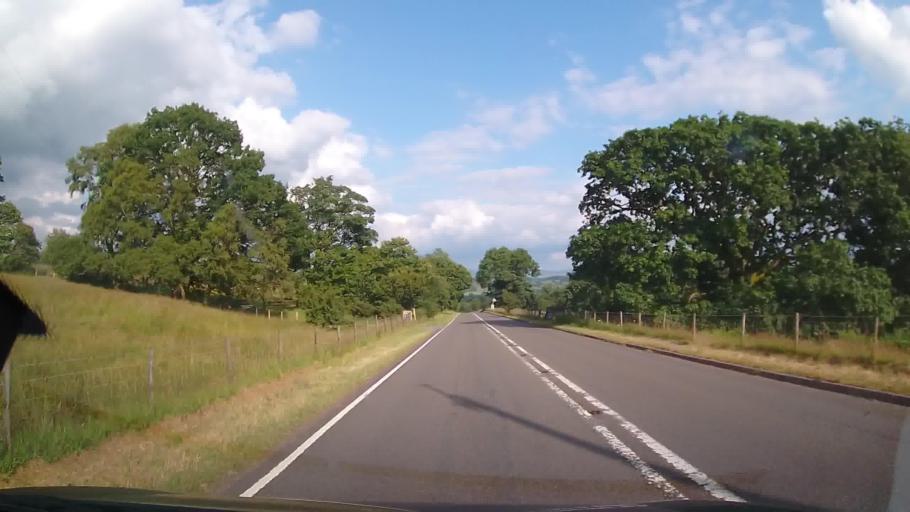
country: GB
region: Wales
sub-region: Gwynedd
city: Bala
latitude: 52.9494
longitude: -3.6617
